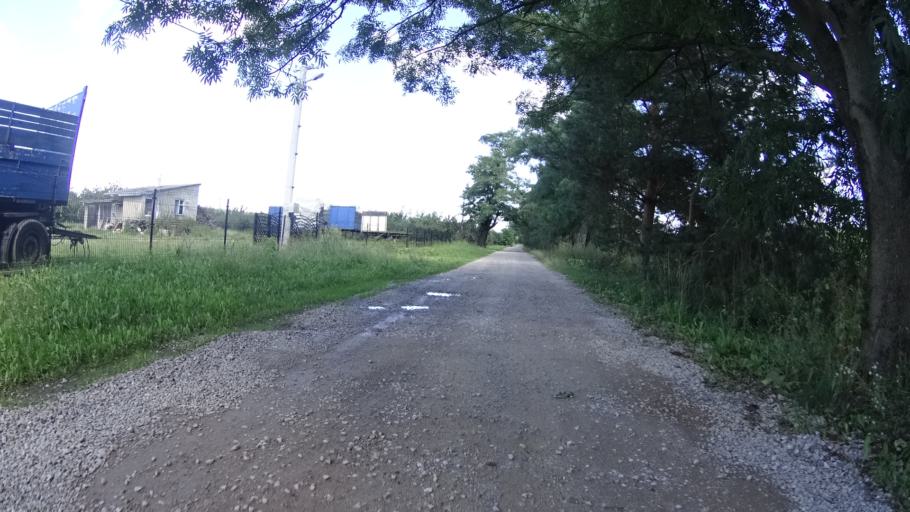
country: PL
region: Masovian Voivodeship
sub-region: Powiat grojecki
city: Mogielnica
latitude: 51.6795
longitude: 20.7597
